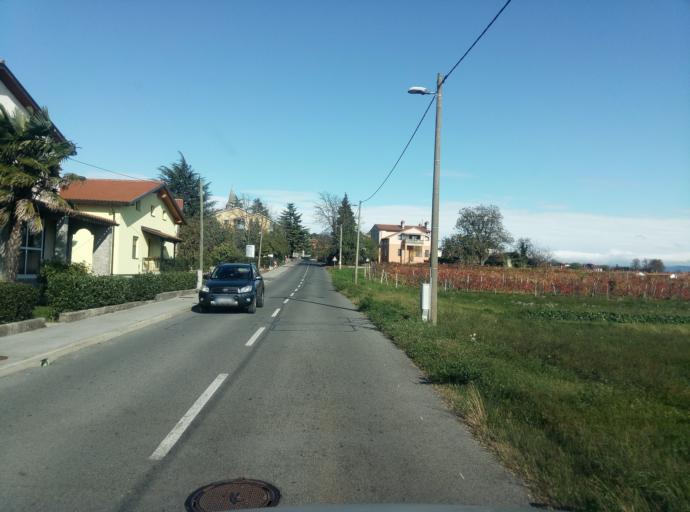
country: SI
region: Komen
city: Komen
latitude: 45.8151
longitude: 13.7427
